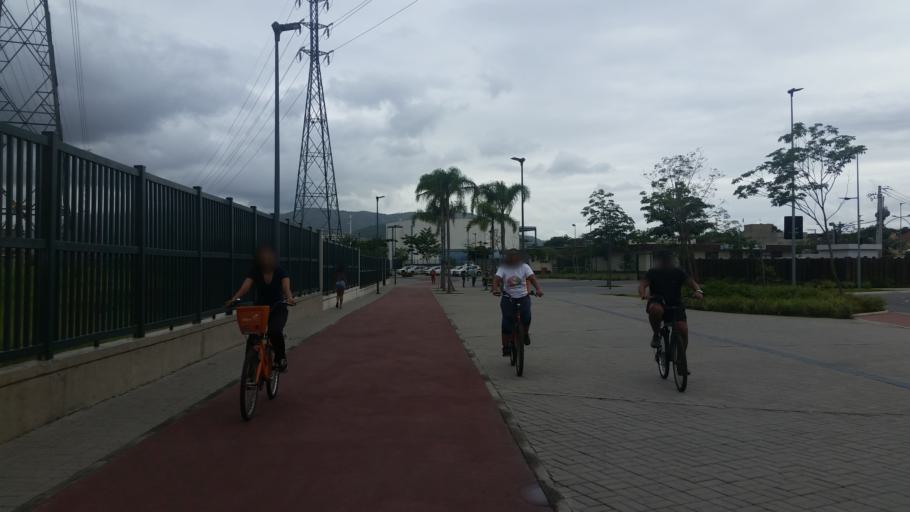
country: BR
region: Rio de Janeiro
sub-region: Sao Joao De Meriti
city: Sao Joao de Meriti
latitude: -22.8601
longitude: -43.3475
